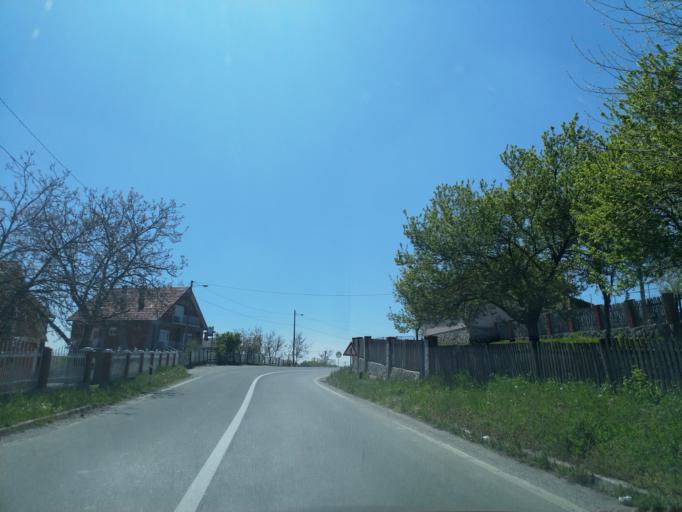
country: RS
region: Central Serbia
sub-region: Belgrade
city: Lazarevac
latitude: 44.3698
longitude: 20.3246
